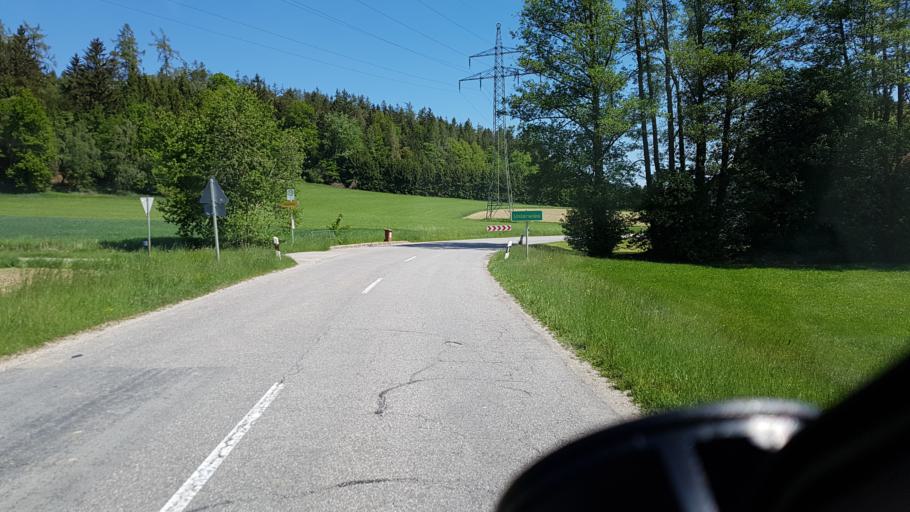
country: DE
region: Bavaria
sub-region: Lower Bavaria
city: Postmunster
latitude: 48.3983
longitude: 12.9271
